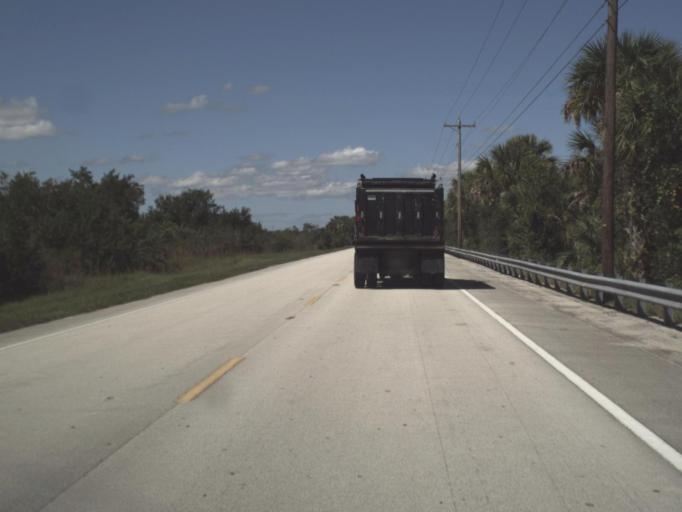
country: US
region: Florida
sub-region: Collier County
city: Marco
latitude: 25.9631
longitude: -81.5223
